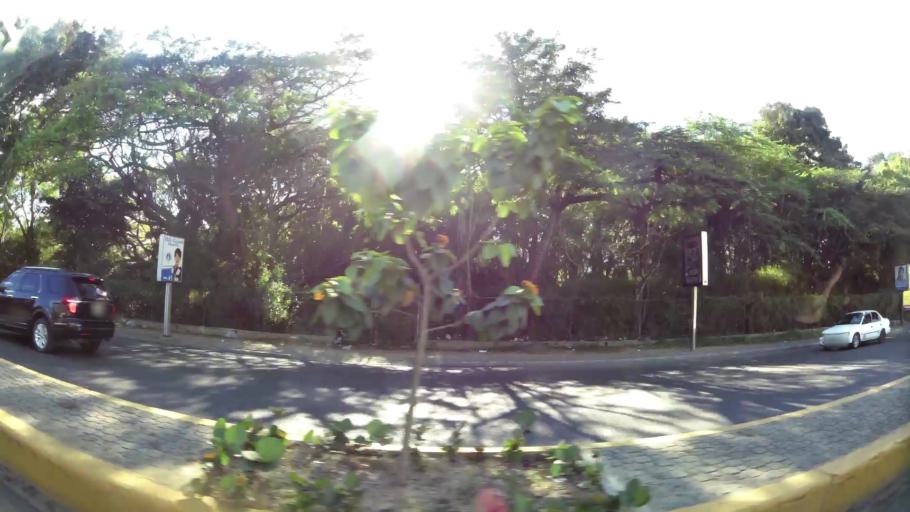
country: DO
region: Santiago
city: Santiago de los Caballeros
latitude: 19.4549
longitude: -70.6852
